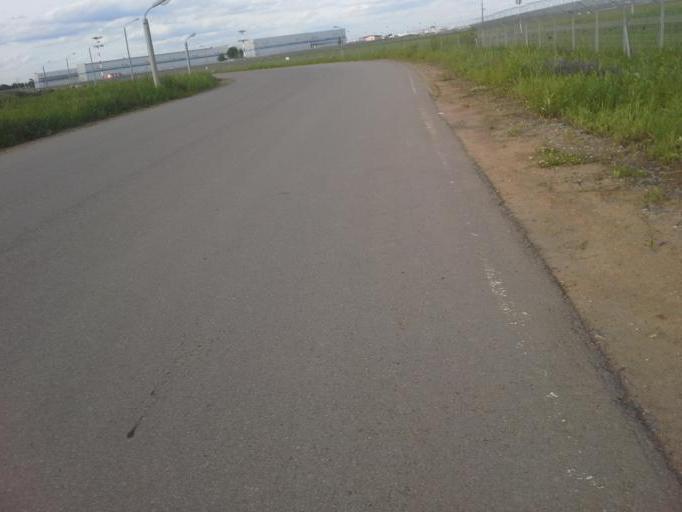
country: RU
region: Moscow
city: Vnukovo
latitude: 55.5865
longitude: 37.2333
